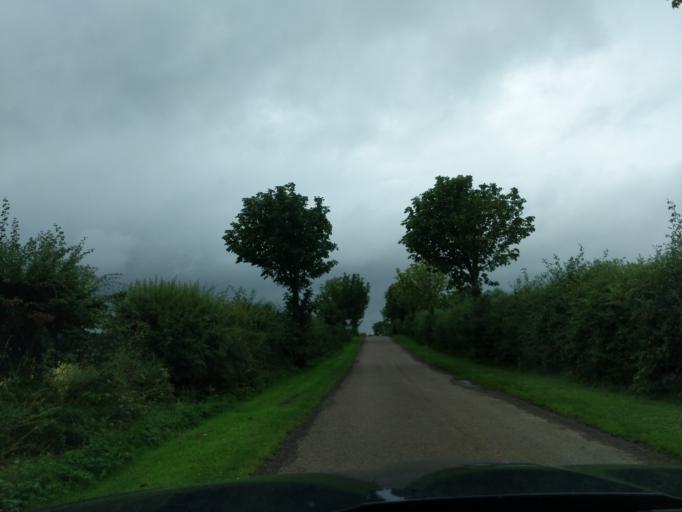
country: GB
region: England
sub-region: Northumberland
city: Ford
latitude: 55.6768
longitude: -2.1169
